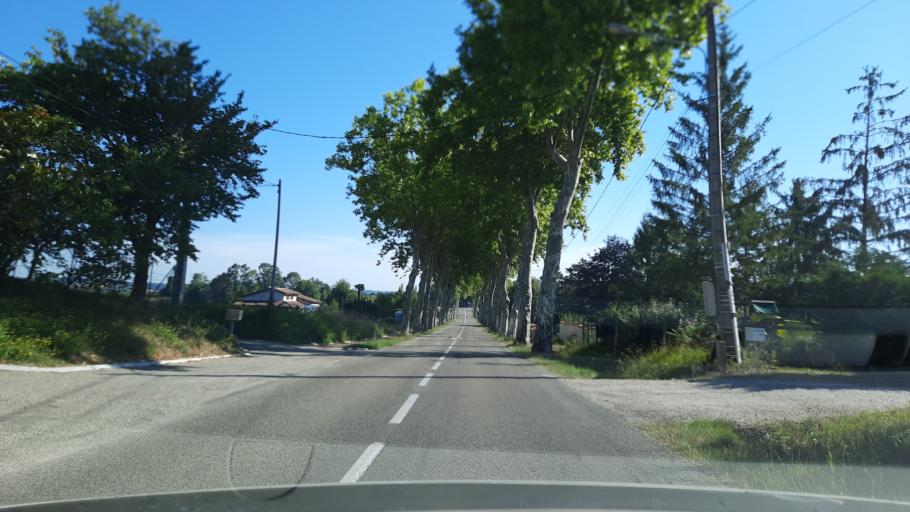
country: FR
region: Midi-Pyrenees
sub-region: Departement du Tarn-et-Garonne
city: Molieres
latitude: 44.1960
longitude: 1.3707
